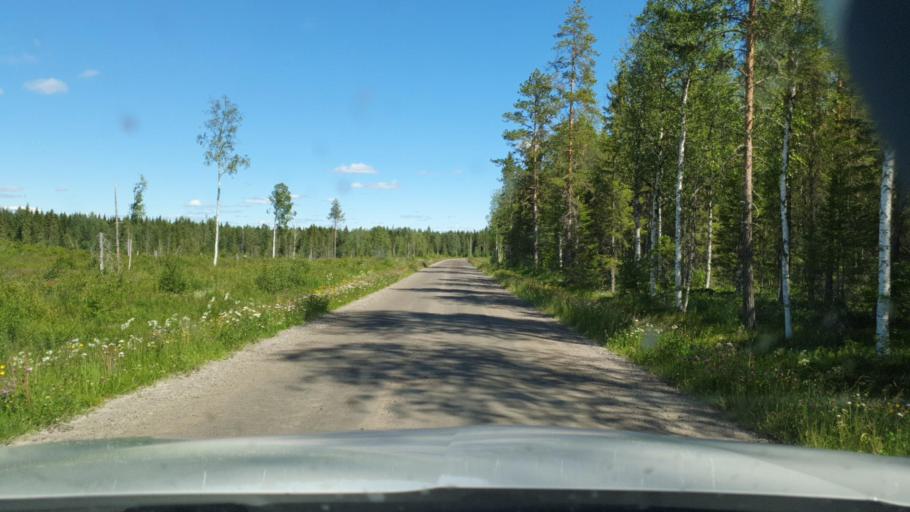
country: SE
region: Vaesterbotten
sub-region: Skelleftea Kommun
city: Byske
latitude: 65.1032
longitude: 21.1719
